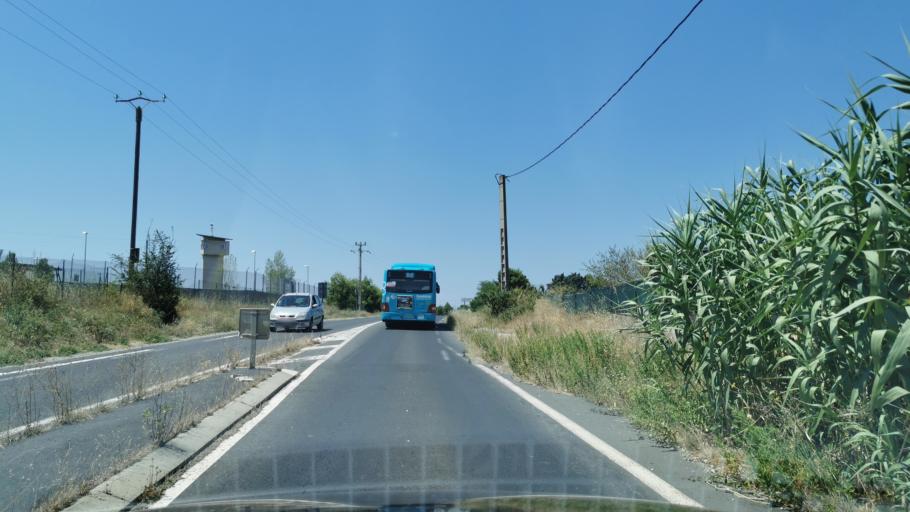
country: FR
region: Languedoc-Roussillon
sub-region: Departement de l'Herault
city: Beziers
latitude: 43.3413
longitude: 3.1829
